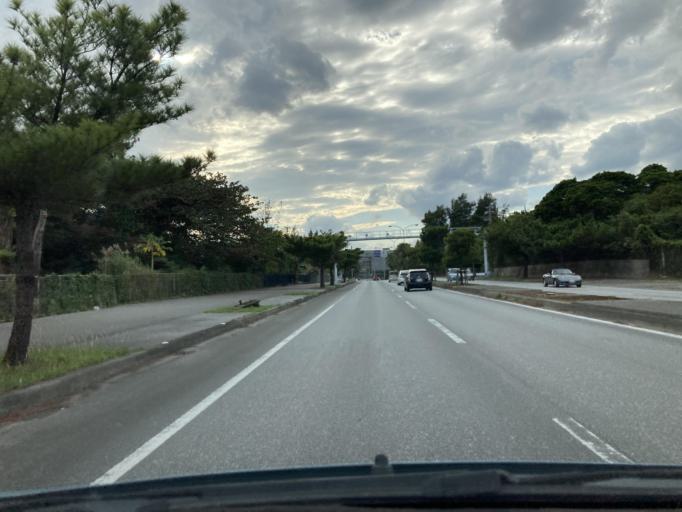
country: JP
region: Okinawa
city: Okinawa
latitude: 26.3686
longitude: 127.7773
